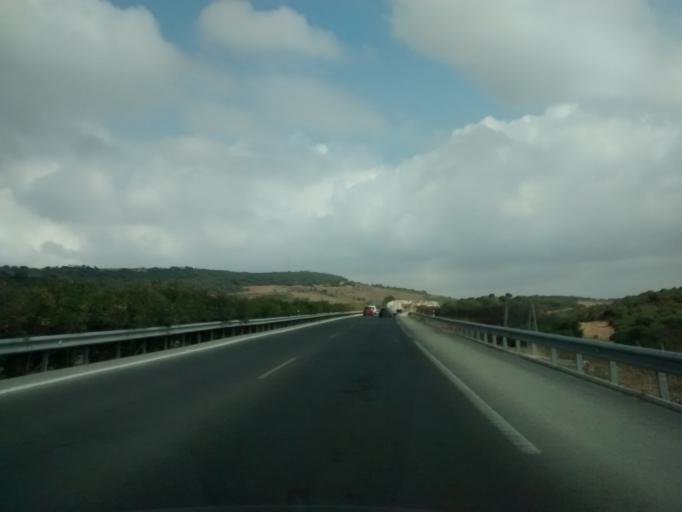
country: ES
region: Andalusia
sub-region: Provincia de Cadiz
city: Conil de la Frontera
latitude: 36.3152
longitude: -6.0571
